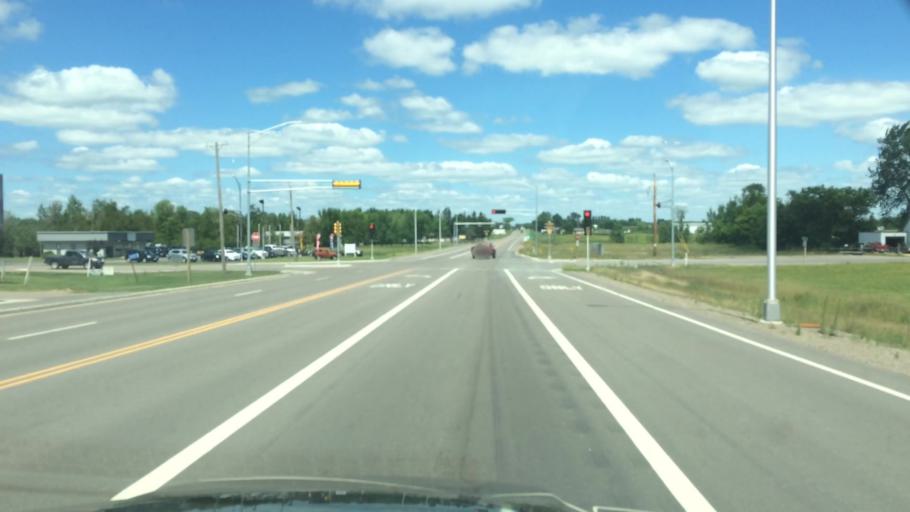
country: US
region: Wisconsin
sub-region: Clark County
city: Abbotsford
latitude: 45.0028
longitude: -90.3157
